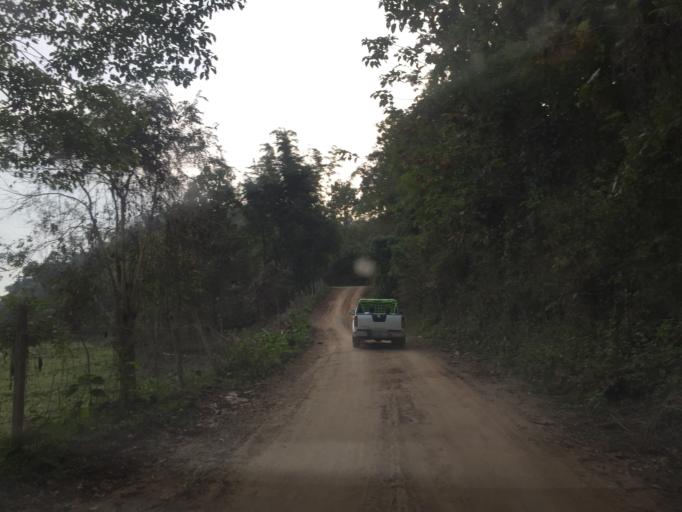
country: TH
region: Chiang Mai
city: Samoeng
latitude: 19.0092
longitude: 98.7305
